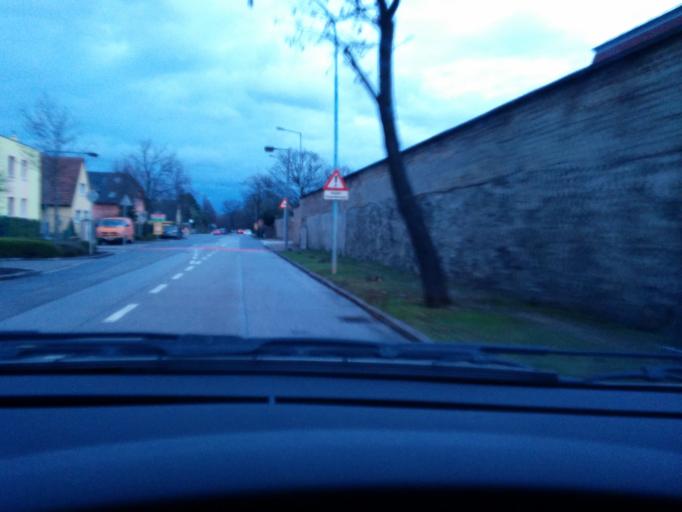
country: AT
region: Lower Austria
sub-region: Politischer Bezirk Modling
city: Wiener Neudorf
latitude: 48.0852
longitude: 16.3229
